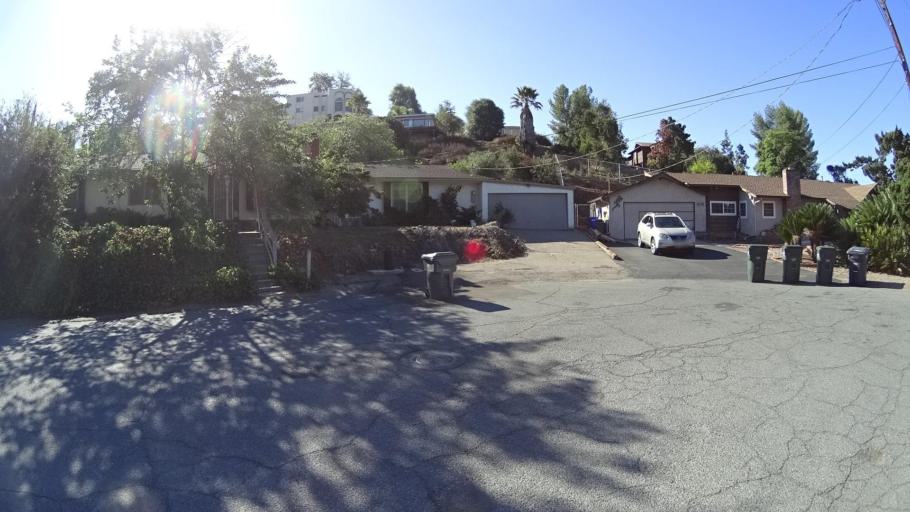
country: US
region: California
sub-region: San Diego County
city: Bostonia
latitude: 32.8184
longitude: -116.9344
